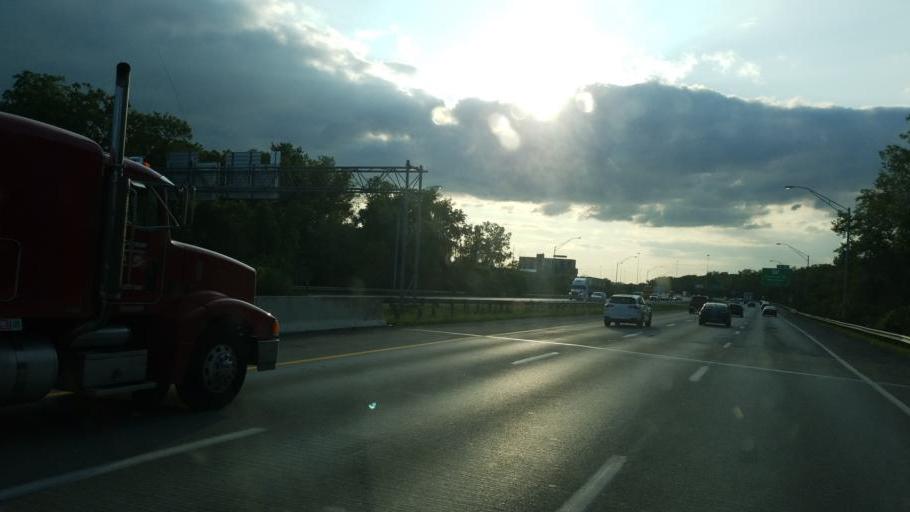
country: US
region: Ohio
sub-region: Franklin County
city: Blacklick Estates
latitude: 39.9357
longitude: -82.8645
